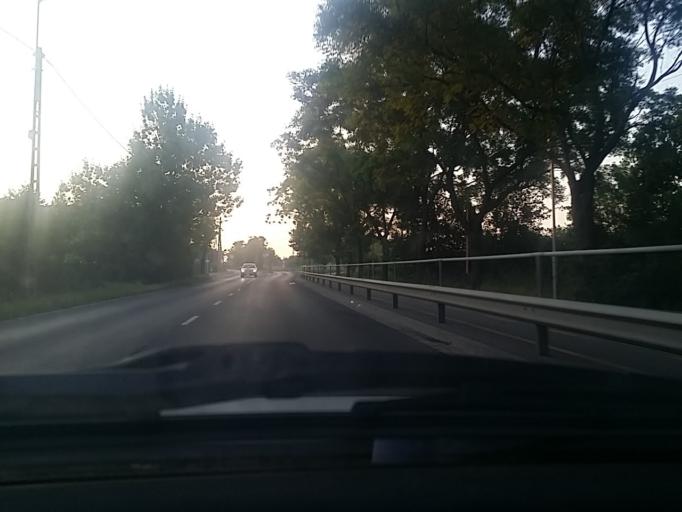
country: HU
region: Budapest
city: Budapest XVII. keruelet
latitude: 47.4717
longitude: 19.2814
